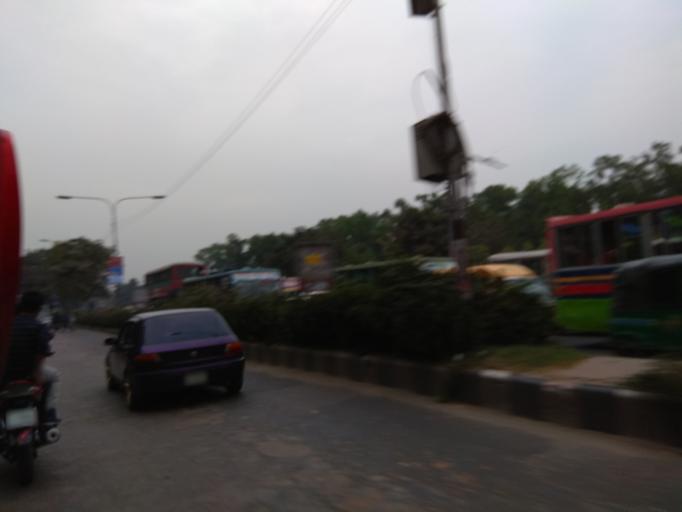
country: BD
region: Dhaka
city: Azimpur
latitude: 23.7654
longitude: 90.3832
